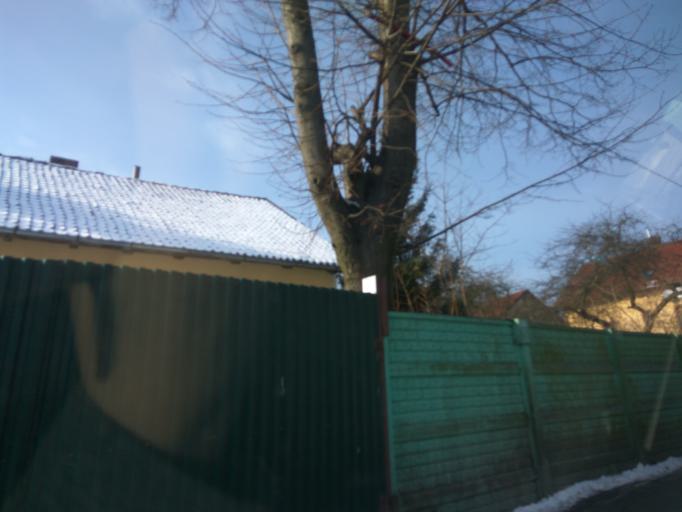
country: RU
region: Kaliningrad
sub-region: Zelenogradskiy Rayon
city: Zelenogradsk
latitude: 54.9590
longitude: 20.4863
